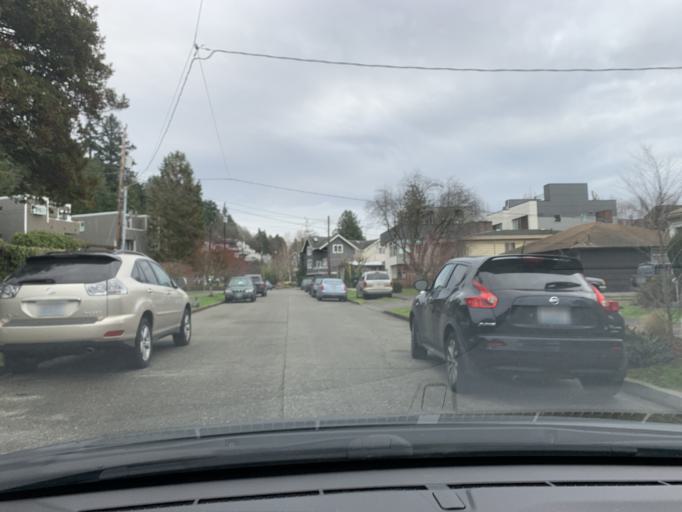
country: US
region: Washington
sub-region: King County
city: White Center
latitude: 47.5673
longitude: -122.4083
